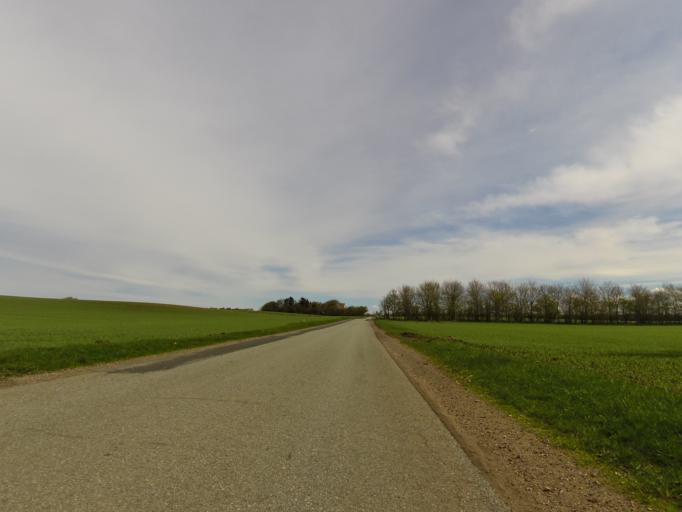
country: DK
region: Central Jutland
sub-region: Holstebro Kommune
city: Vinderup
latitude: 56.5353
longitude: 8.9052
